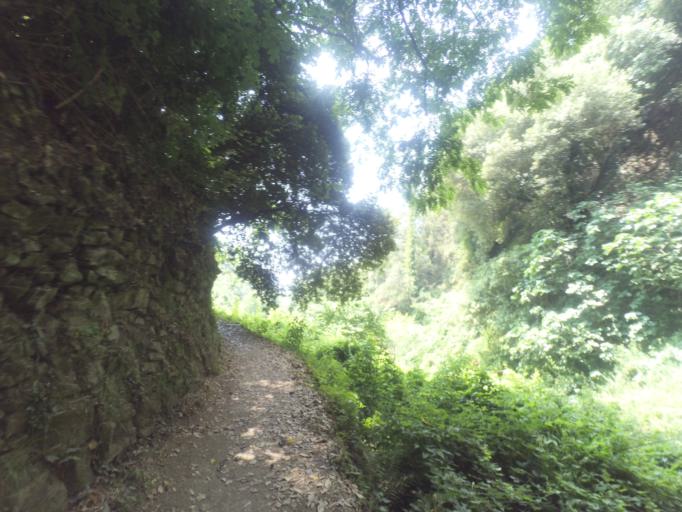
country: IT
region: Liguria
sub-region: Provincia di La Spezia
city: Riomaggiore
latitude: 44.1249
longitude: 9.7232
